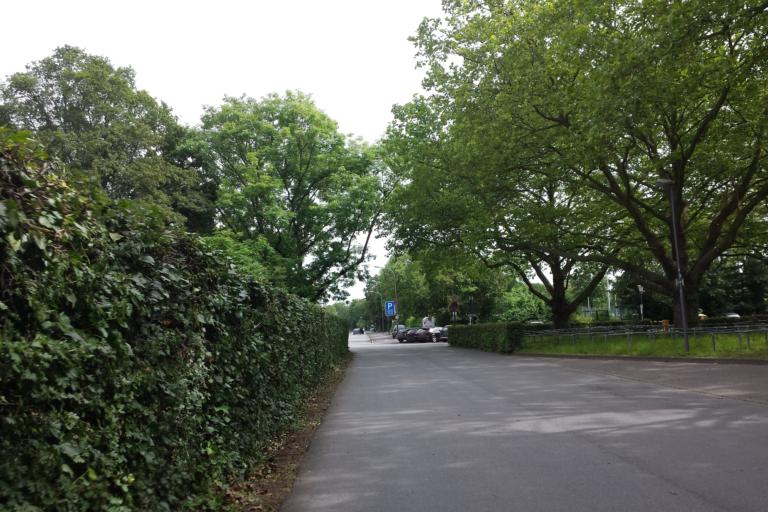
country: DE
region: Baden-Wuerttemberg
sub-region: Karlsruhe Region
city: Eppelheim
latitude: 49.4203
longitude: 8.6595
